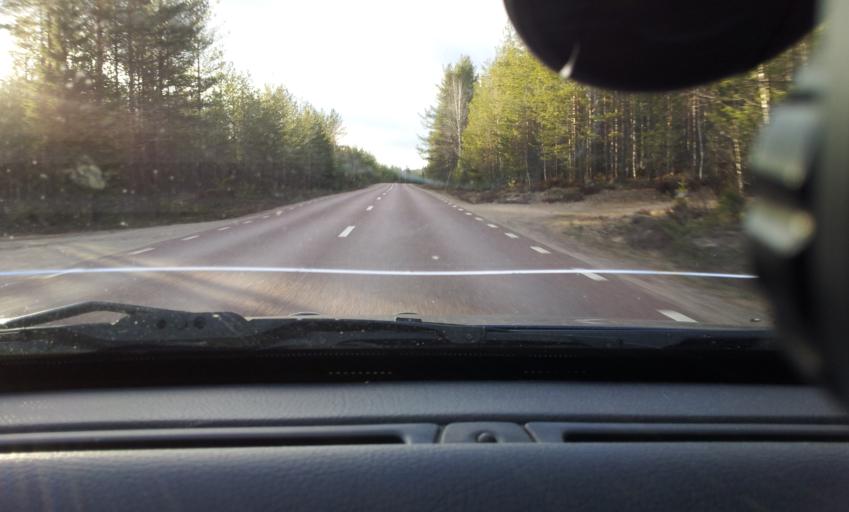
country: SE
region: Jaemtland
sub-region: Harjedalens Kommun
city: Sveg
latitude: 62.1855
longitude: 14.8690
